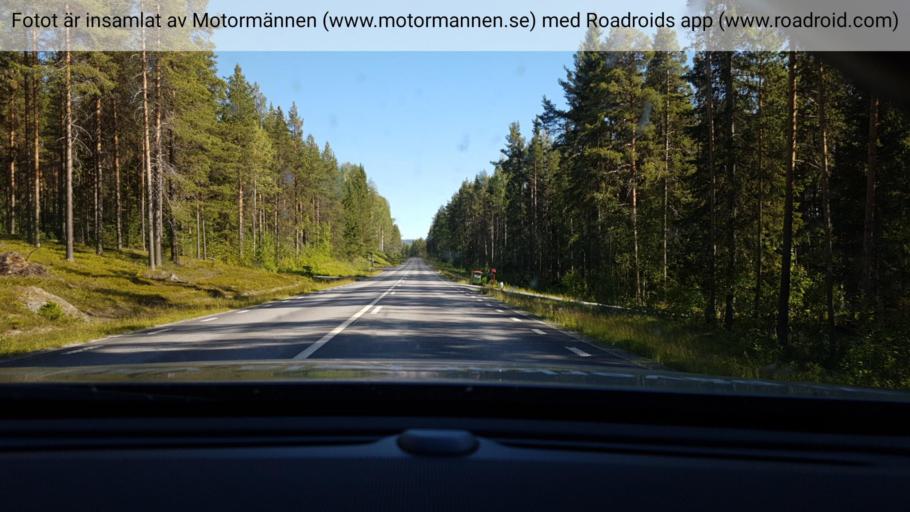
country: SE
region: Vaesterbotten
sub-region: Lycksele Kommun
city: Lycksele
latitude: 64.5561
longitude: 18.7304
